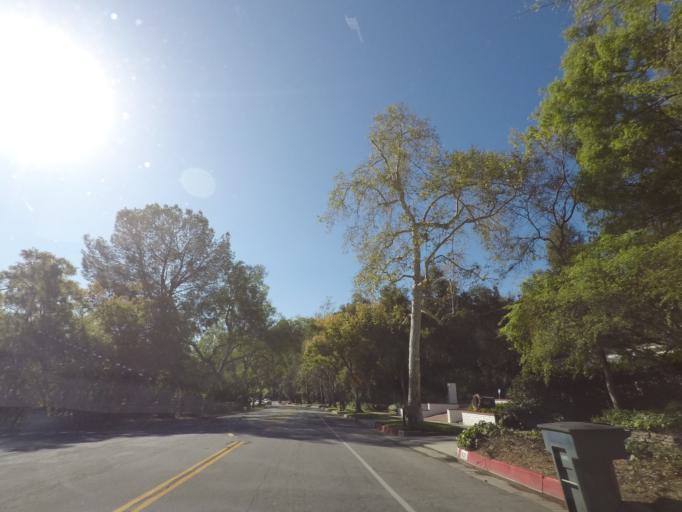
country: US
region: California
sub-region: Los Angeles County
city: Pasadena
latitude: 34.1561
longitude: -118.1718
